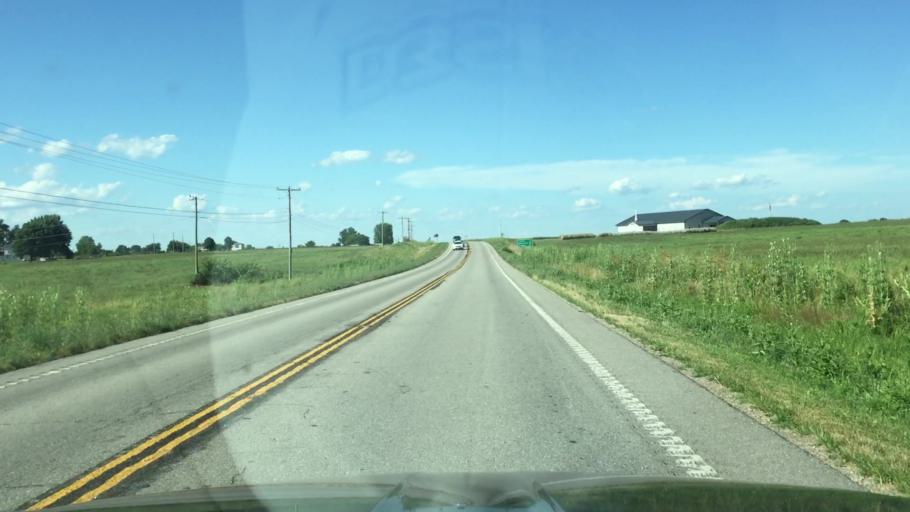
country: US
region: Missouri
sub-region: Moniteau County
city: Tipton
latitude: 38.5705
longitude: -92.7961
